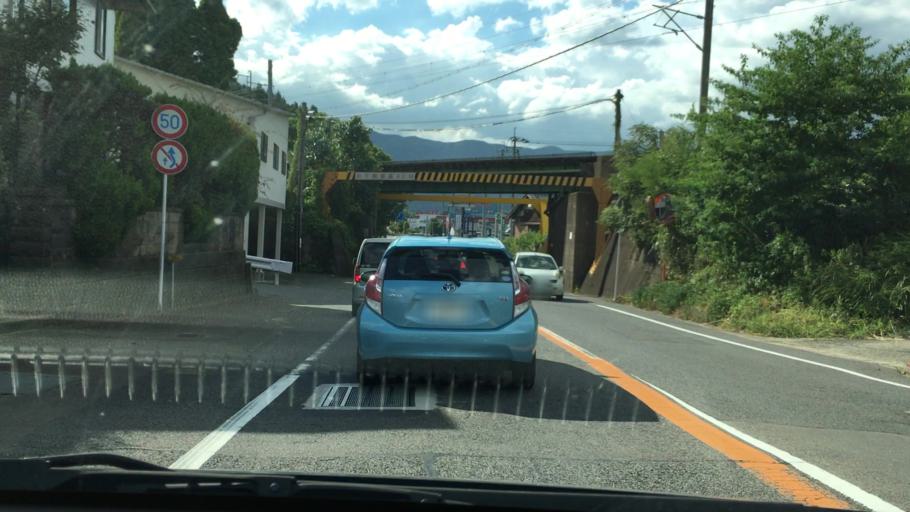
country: JP
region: Saga Prefecture
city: Imaricho-ko
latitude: 33.1879
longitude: 129.8649
